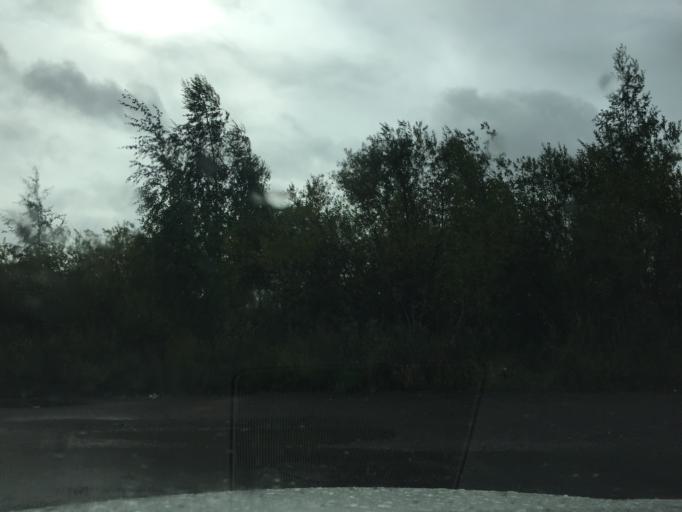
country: RU
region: St.-Petersburg
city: Sosnovaya Polyana
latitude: 59.8555
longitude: 30.1264
